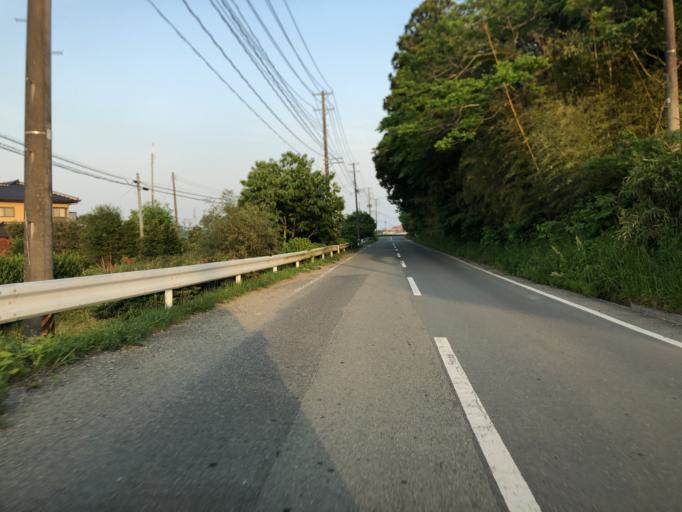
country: JP
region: Fukushima
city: Namie
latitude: 37.2717
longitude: 140.9883
